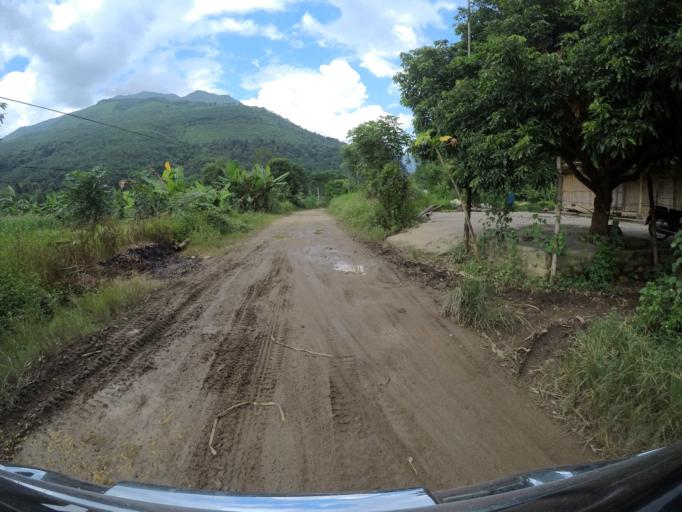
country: VN
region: Yen Bai
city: Son Thinh
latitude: 21.6655
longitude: 104.5126
